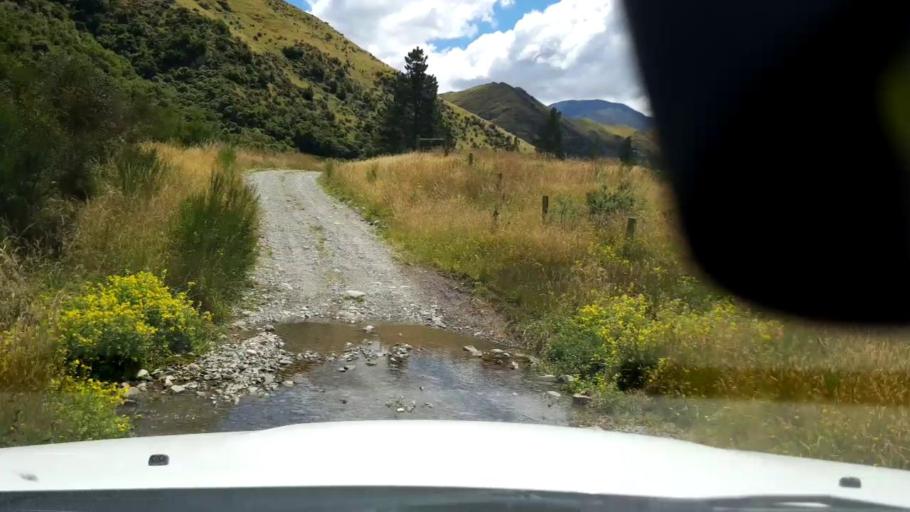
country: NZ
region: Canterbury
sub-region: Timaru District
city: Pleasant Point
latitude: -43.9301
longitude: 171.1922
